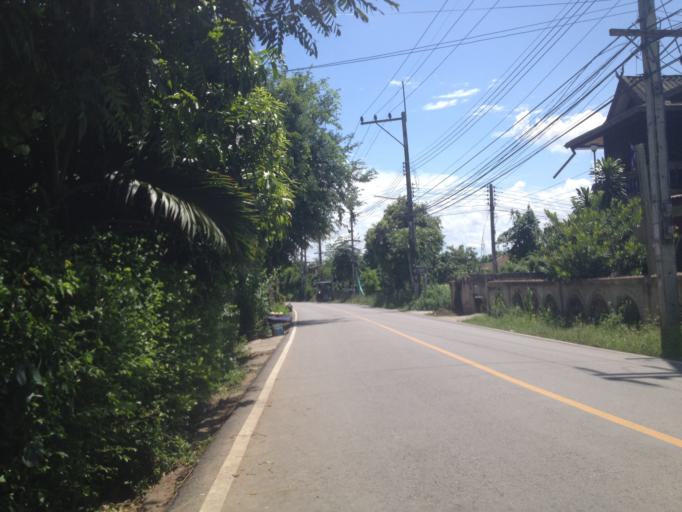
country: TH
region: Chiang Mai
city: Hang Dong
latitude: 18.6841
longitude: 98.9273
